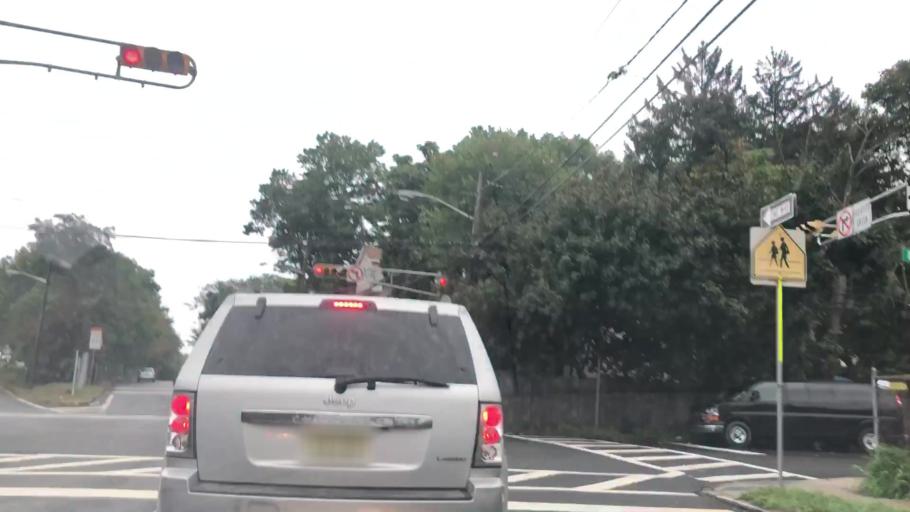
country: US
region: New Jersey
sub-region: Essex County
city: Irvington
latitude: 40.7423
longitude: -74.2140
